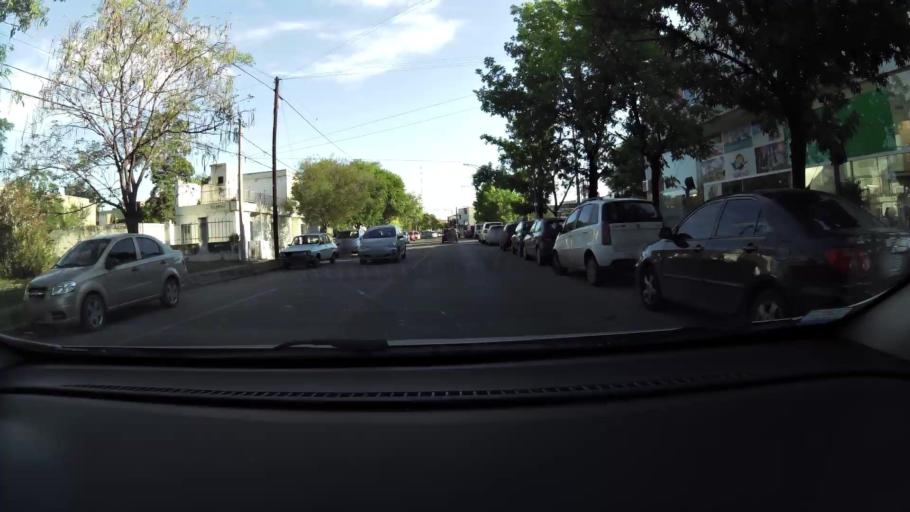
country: AR
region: Cordoba
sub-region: Departamento de Capital
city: Cordoba
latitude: -31.3721
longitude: -64.2265
